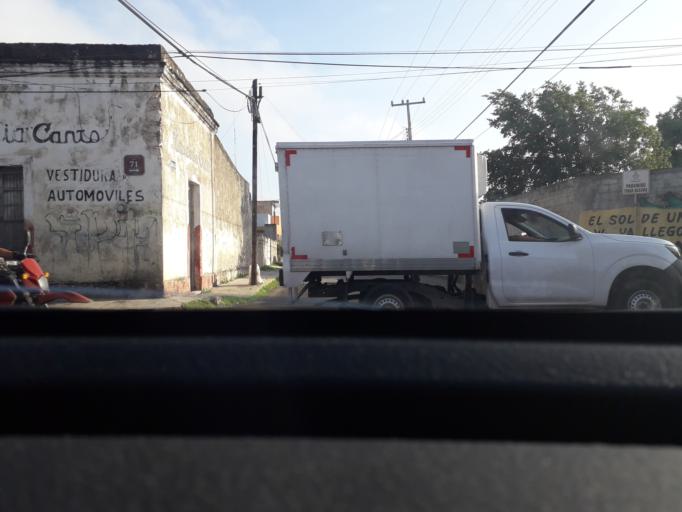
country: MX
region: Yucatan
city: Merida
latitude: 20.9623
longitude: -89.6350
